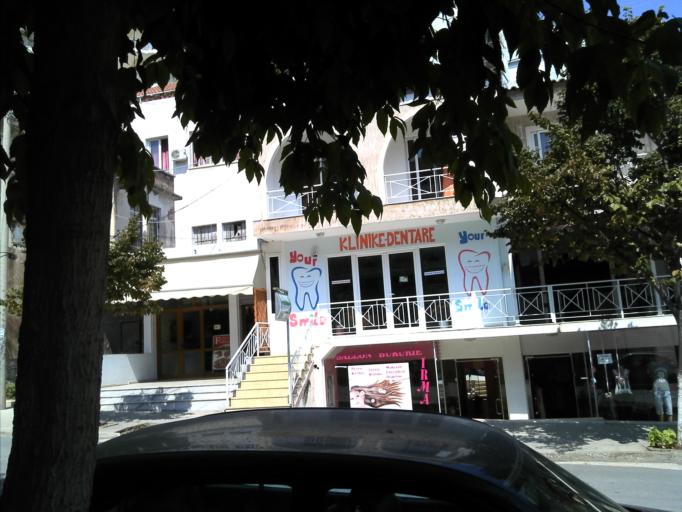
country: AL
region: Vlore
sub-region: Rrethi i Sarandes
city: Sarande
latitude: 39.8733
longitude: 20.0016
